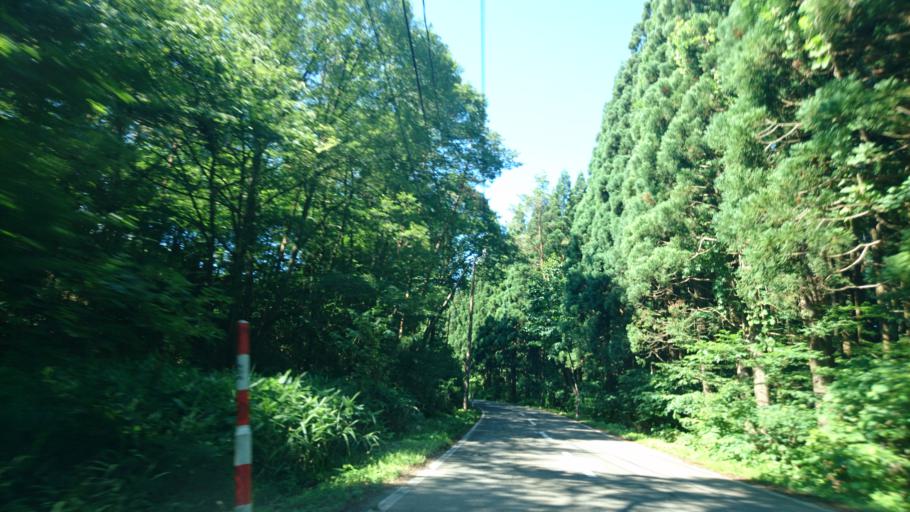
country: JP
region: Akita
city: Kakunodatemachi
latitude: 39.7249
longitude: 140.6994
